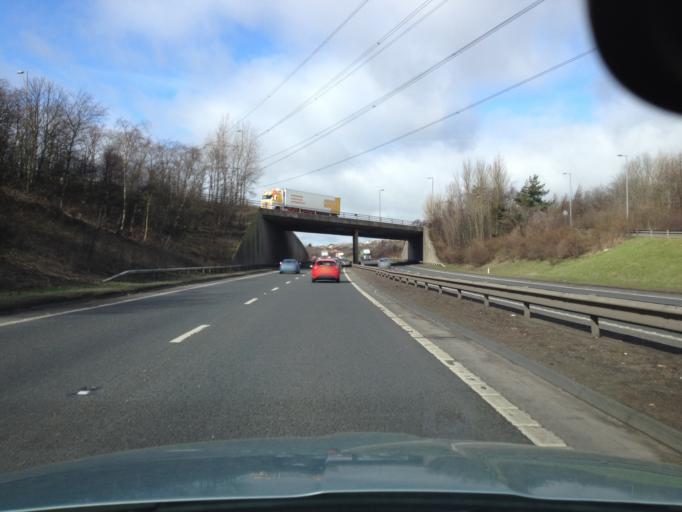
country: GB
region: Scotland
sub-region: Midlothian
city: Loanhead
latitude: 55.8950
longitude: -3.2010
